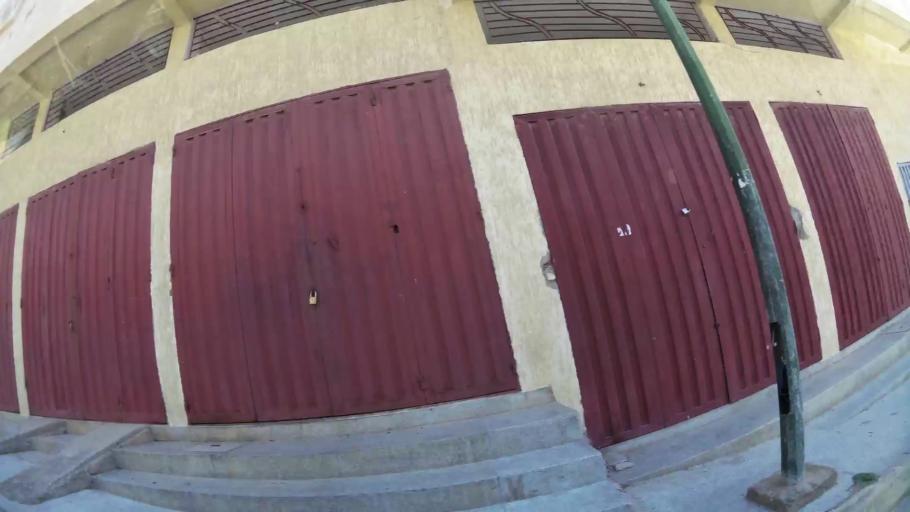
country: MA
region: Fes-Boulemane
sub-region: Fes
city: Fes
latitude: 34.0611
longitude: -5.0297
